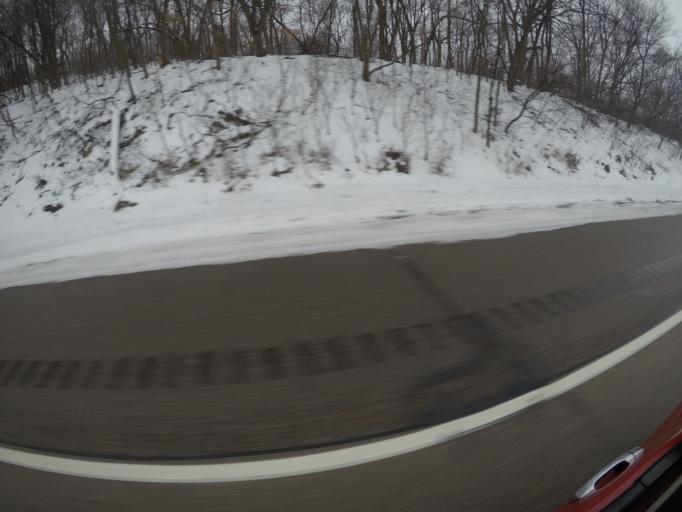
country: US
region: Minnesota
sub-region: Goodhue County
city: Cannon Falls
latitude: 44.4464
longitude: -92.8946
